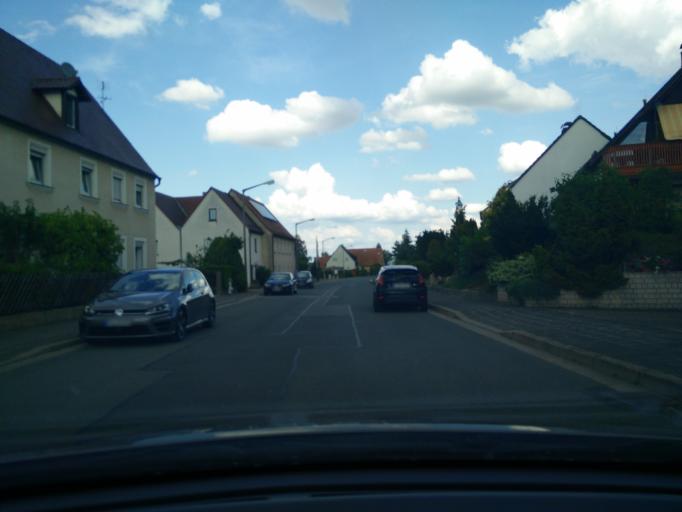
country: DE
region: Bavaria
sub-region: Regierungsbezirk Mittelfranken
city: Stein
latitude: 49.3918
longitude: 10.9916
